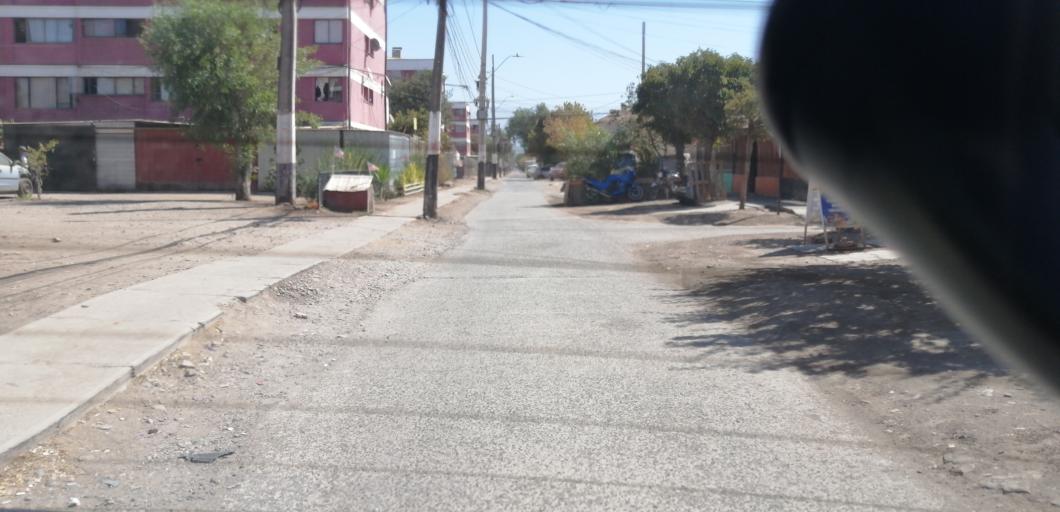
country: CL
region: Santiago Metropolitan
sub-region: Provincia de Santiago
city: Lo Prado
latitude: -33.4512
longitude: -70.7429
